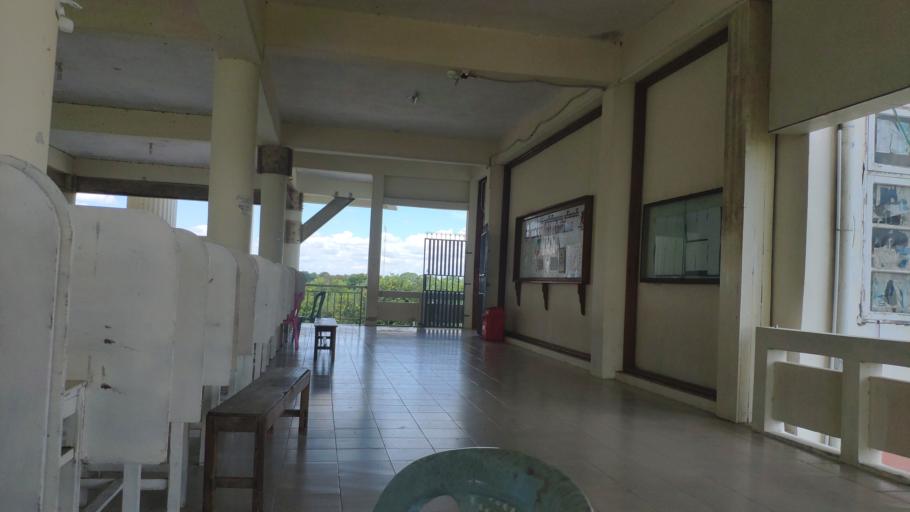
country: MM
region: Mandalay
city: Meiktila
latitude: 20.9131
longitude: 95.8594
